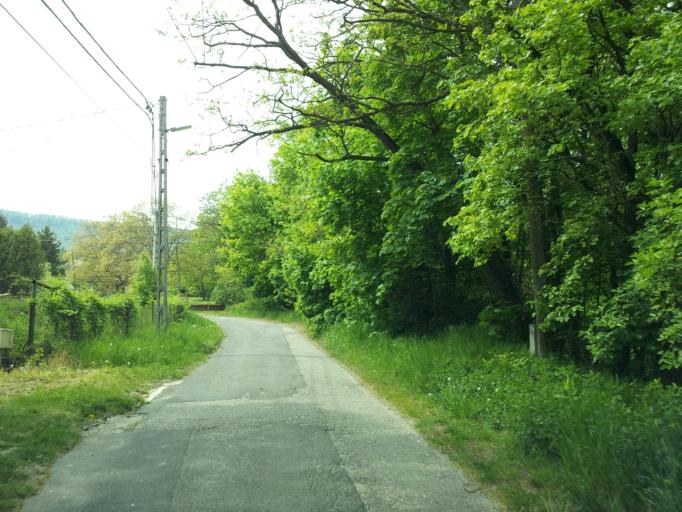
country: HU
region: Pest
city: Tahitotfalu
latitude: 47.7519
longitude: 19.0688
